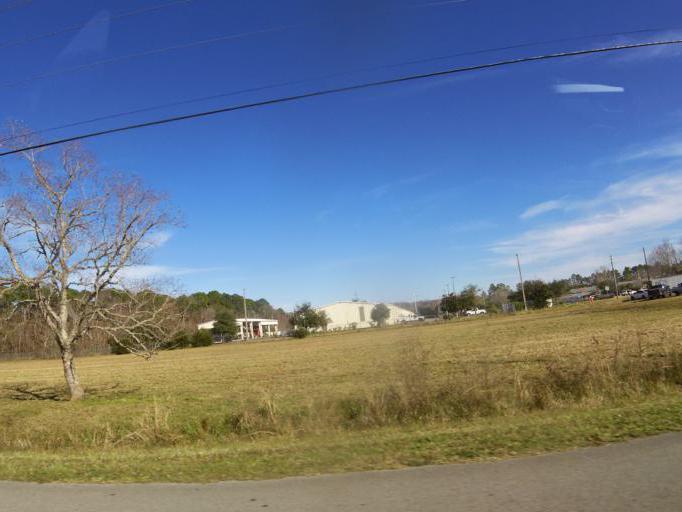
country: US
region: Florida
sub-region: Saint Johns County
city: Saint Augustine
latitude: 29.9212
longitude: -81.4033
